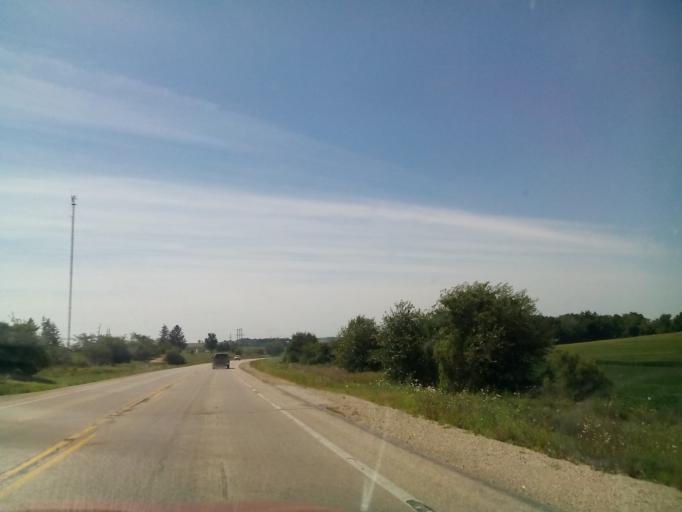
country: US
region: Wisconsin
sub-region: Green County
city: Monroe
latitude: 42.6728
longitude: -89.6174
